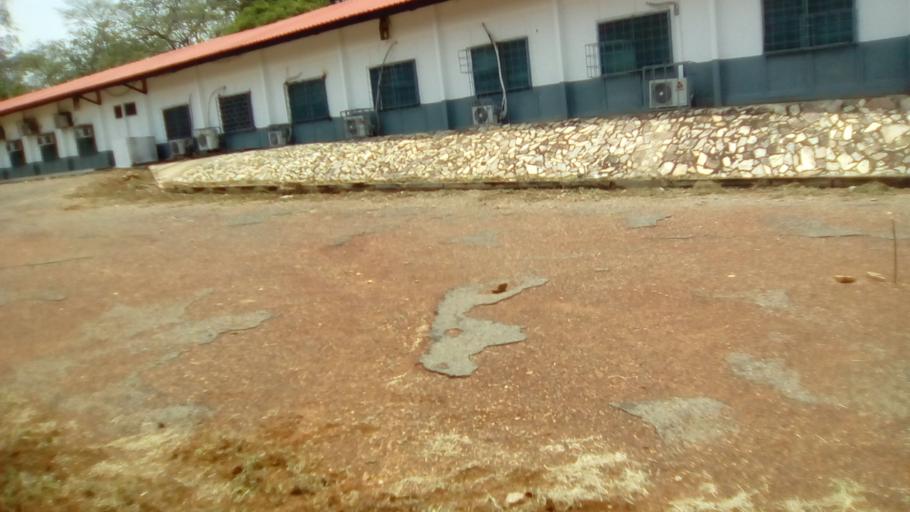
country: GH
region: Greater Accra
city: Medina Estates
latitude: 5.6550
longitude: -0.1862
